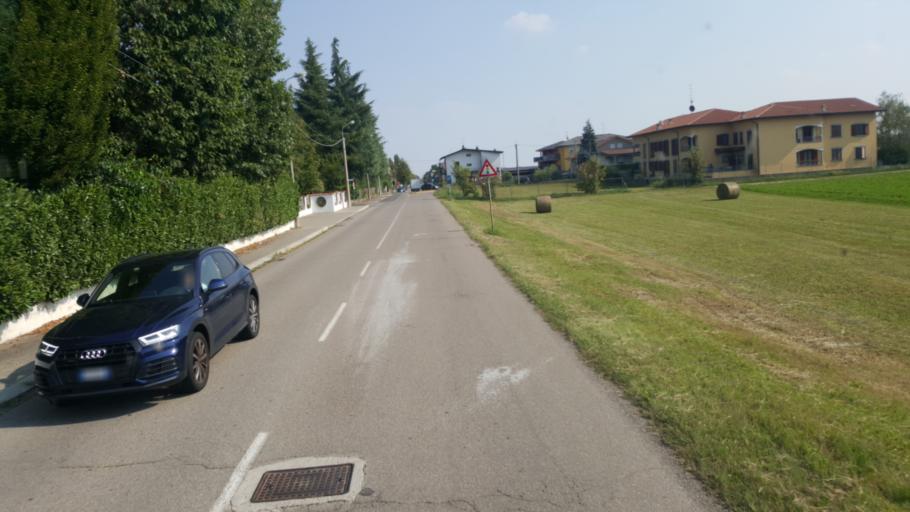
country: IT
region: Lombardy
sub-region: Provincia di Como
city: Mozzate
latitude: 45.6743
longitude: 8.9448
